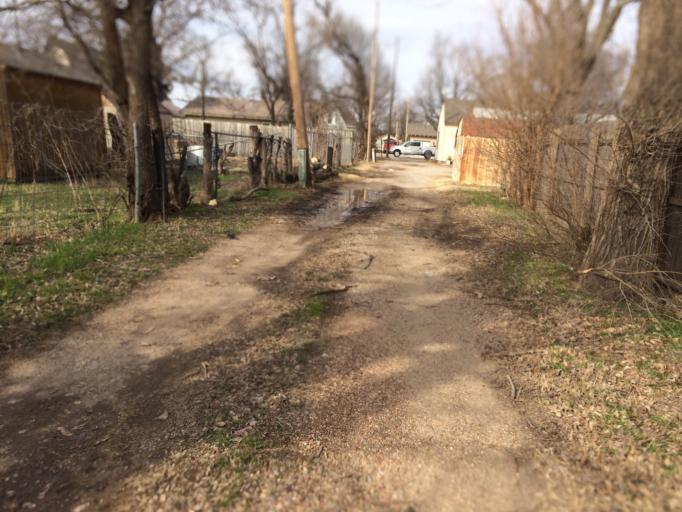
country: US
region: Oklahoma
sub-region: Cleveland County
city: Norman
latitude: 35.2271
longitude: -97.4352
